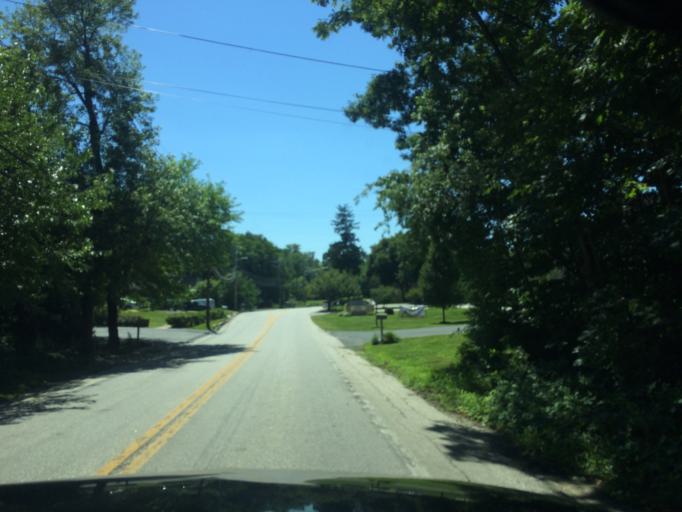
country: US
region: Maryland
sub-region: Baltimore County
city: Lutherville
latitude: 39.4203
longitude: -76.6208
